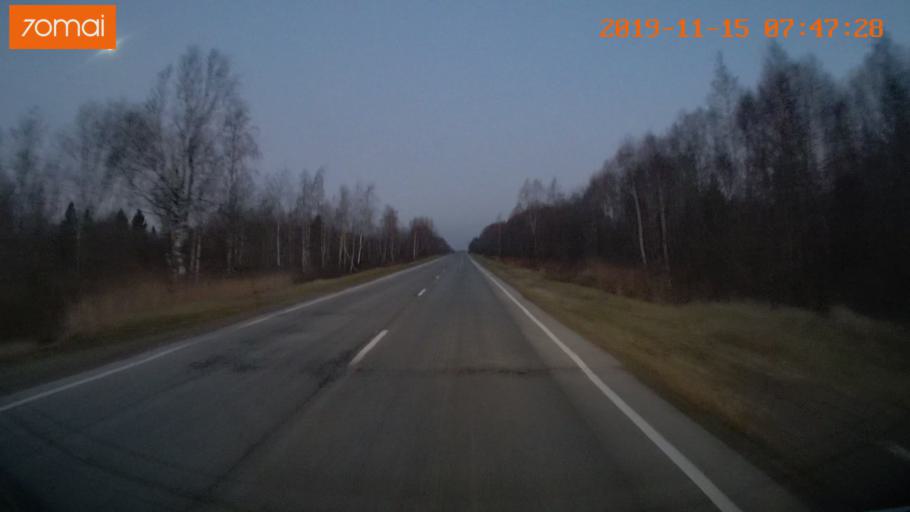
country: RU
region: Vologda
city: Sheksna
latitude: 58.8418
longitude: 38.2604
